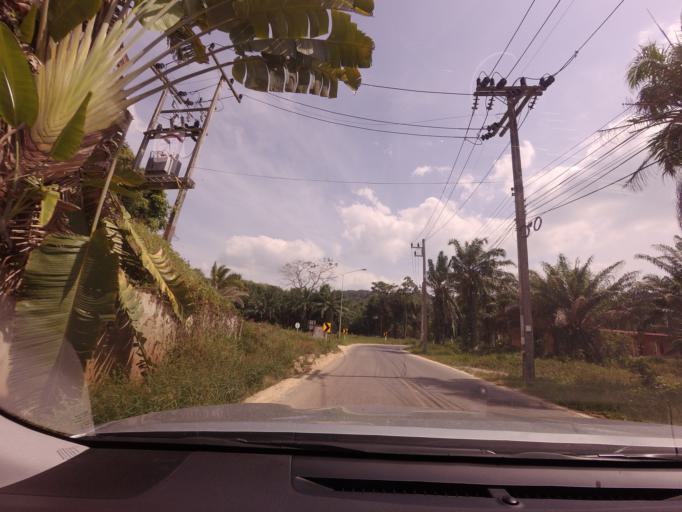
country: TH
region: Phangnga
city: Ban Ao Nang
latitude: 8.0759
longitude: 98.7458
